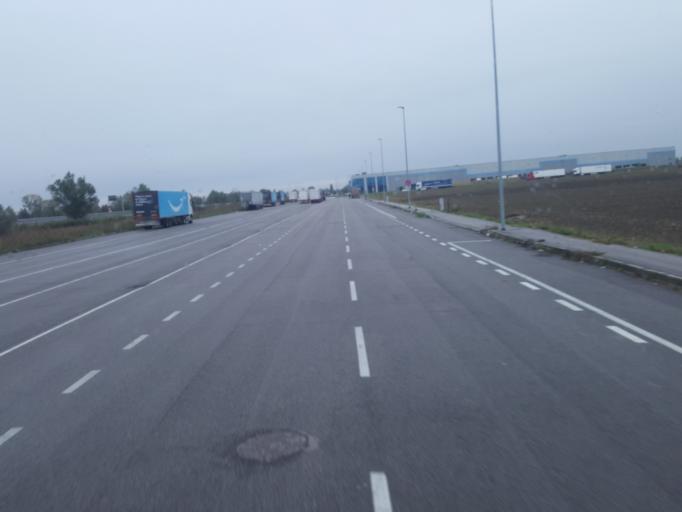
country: IT
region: Veneto
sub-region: Provincia di Rovigo
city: Villamarzana
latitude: 45.0194
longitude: 11.7066
